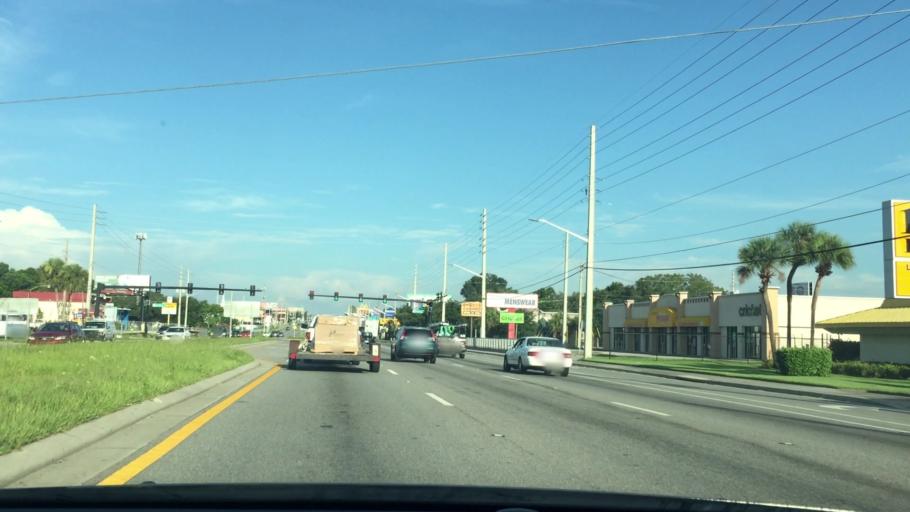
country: US
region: Florida
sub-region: Orange County
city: Pine Hills
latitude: 28.5526
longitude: -81.4585
